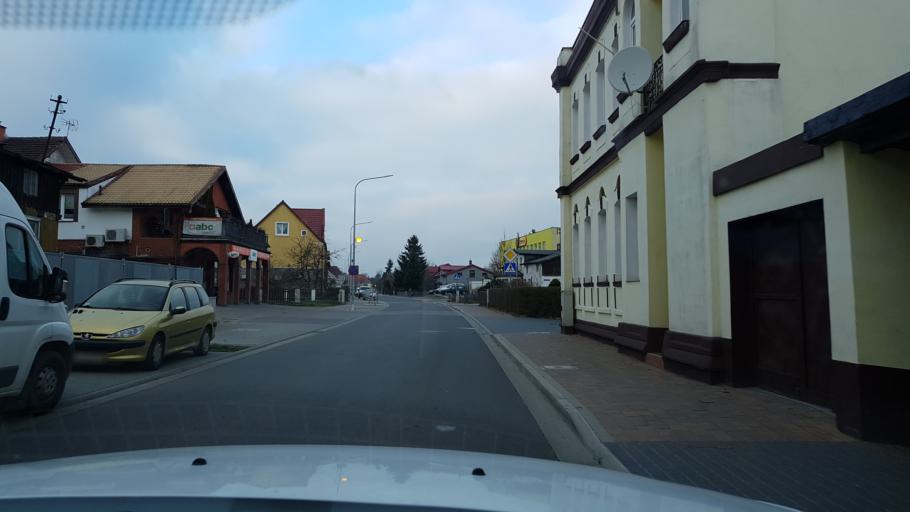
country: PL
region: West Pomeranian Voivodeship
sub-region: Powiat kolobrzeski
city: Goscino
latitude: 54.0493
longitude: 15.6545
